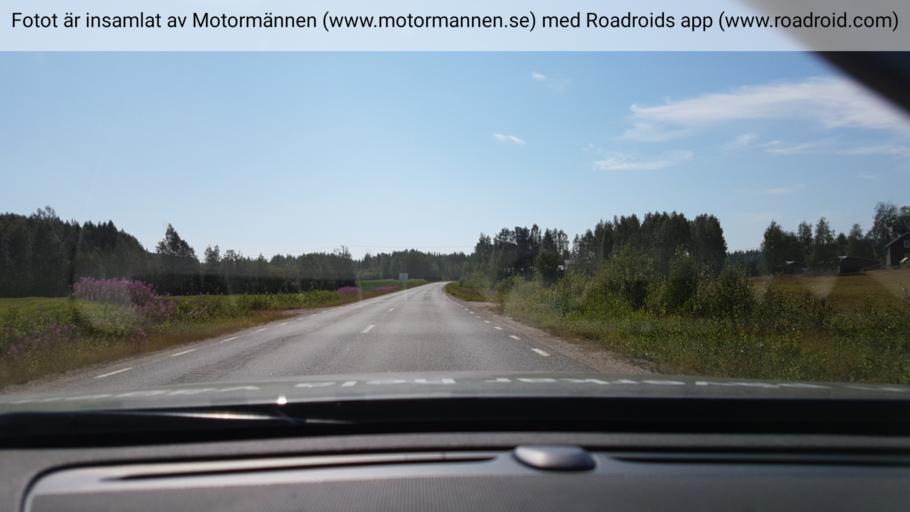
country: SE
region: Vaesterbotten
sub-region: Vindelns Kommun
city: Vindeln
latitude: 64.2935
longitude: 19.6203
